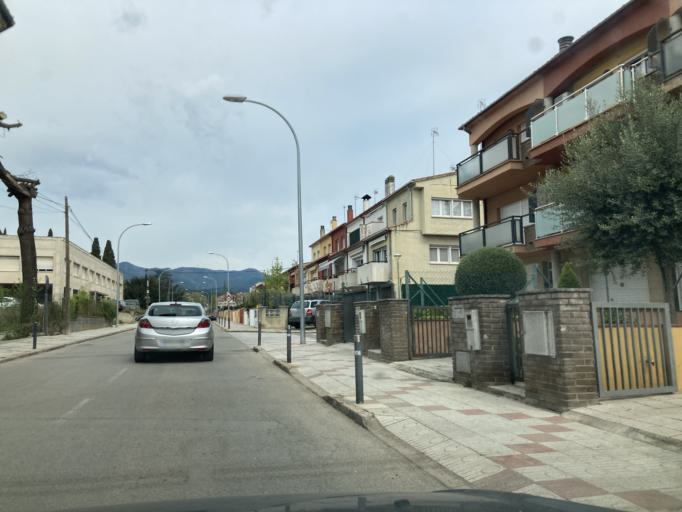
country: ES
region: Catalonia
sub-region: Provincia de Girona
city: Santa Coloma de Farners
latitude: 41.8647
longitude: 2.6592
